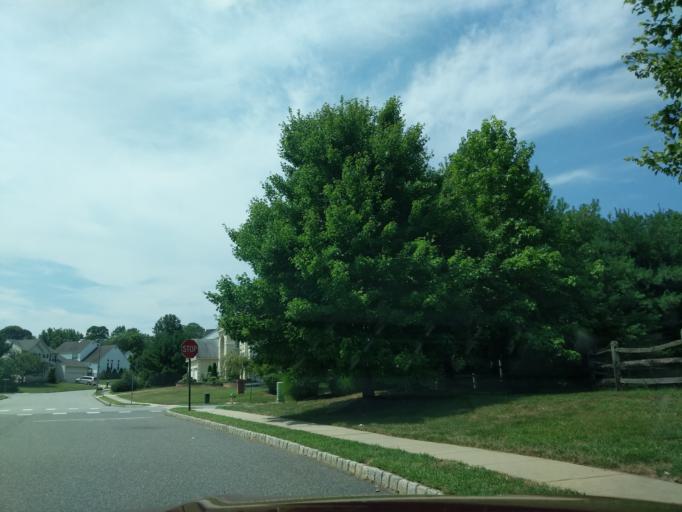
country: US
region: New Jersey
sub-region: Gloucester County
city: Westville
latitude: 39.8353
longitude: -75.1142
